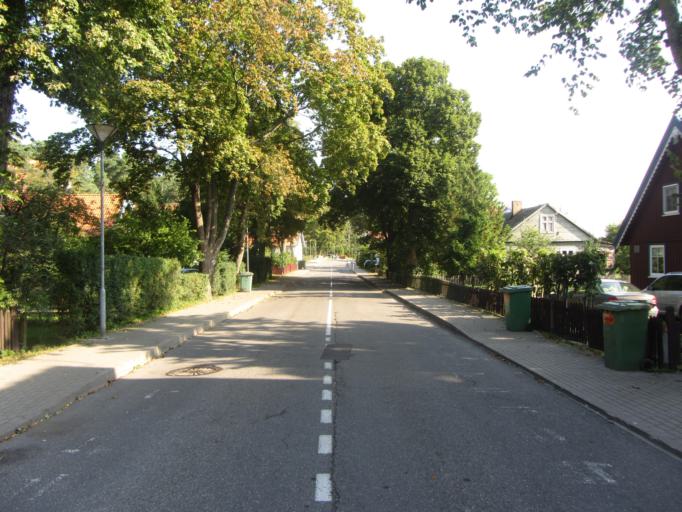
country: LT
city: Nida
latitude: 55.3081
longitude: 21.0039
